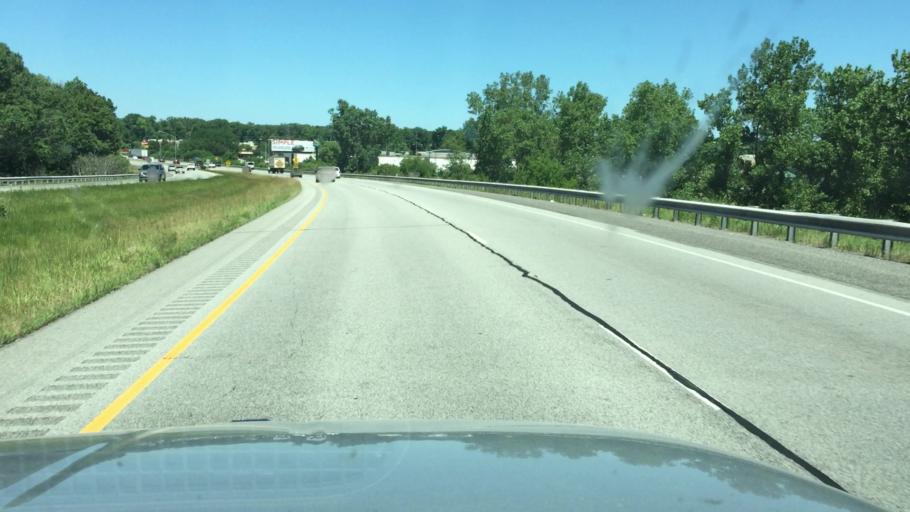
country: US
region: Indiana
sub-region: Porter County
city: Chesterton
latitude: 41.6118
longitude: -87.0405
